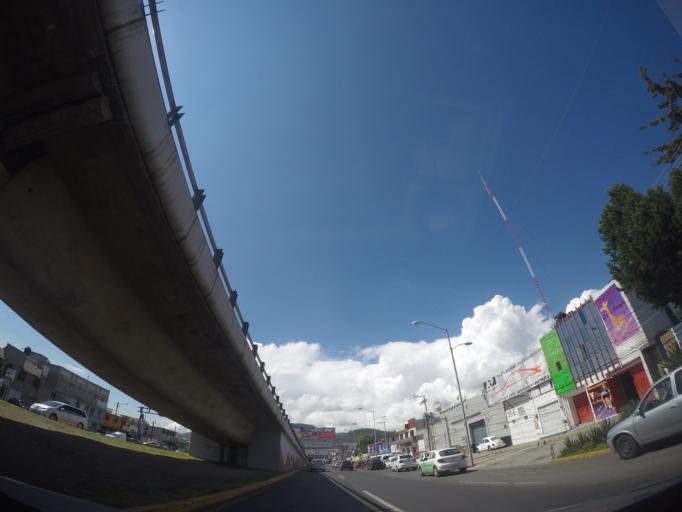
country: MX
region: Hidalgo
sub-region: Mineral de la Reforma
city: Unidad Minera 11 de Julio
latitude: 20.1062
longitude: -98.7203
